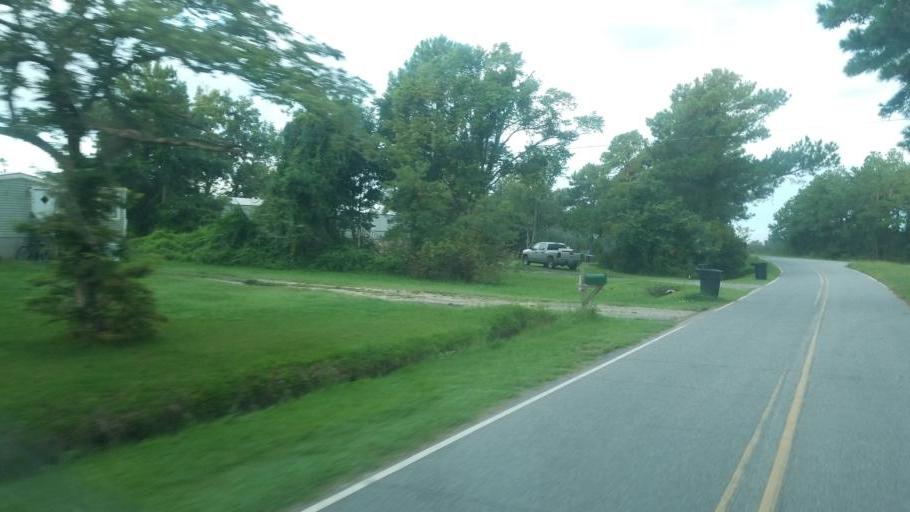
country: US
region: North Carolina
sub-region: Dare County
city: Wanchese
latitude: 35.8417
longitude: -75.6544
